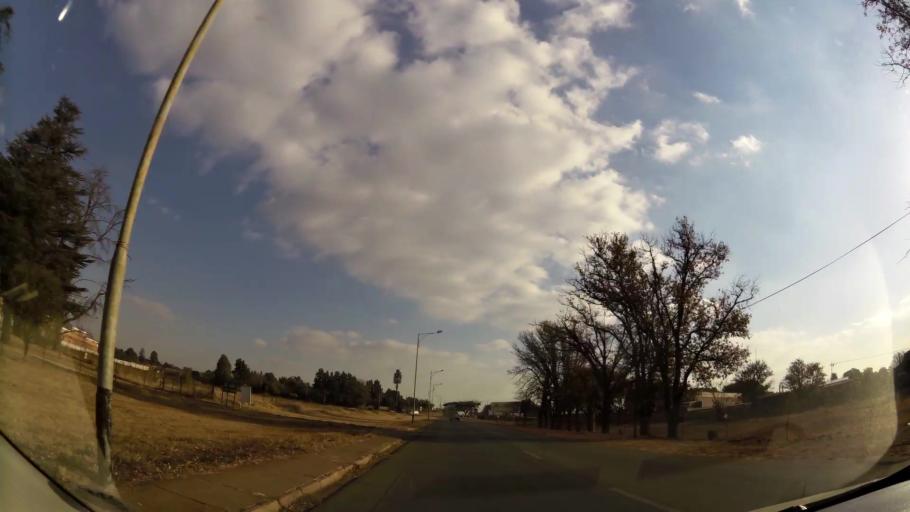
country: ZA
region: Gauteng
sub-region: West Rand District Municipality
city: Krugersdorp
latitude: -26.1001
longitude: 27.7405
